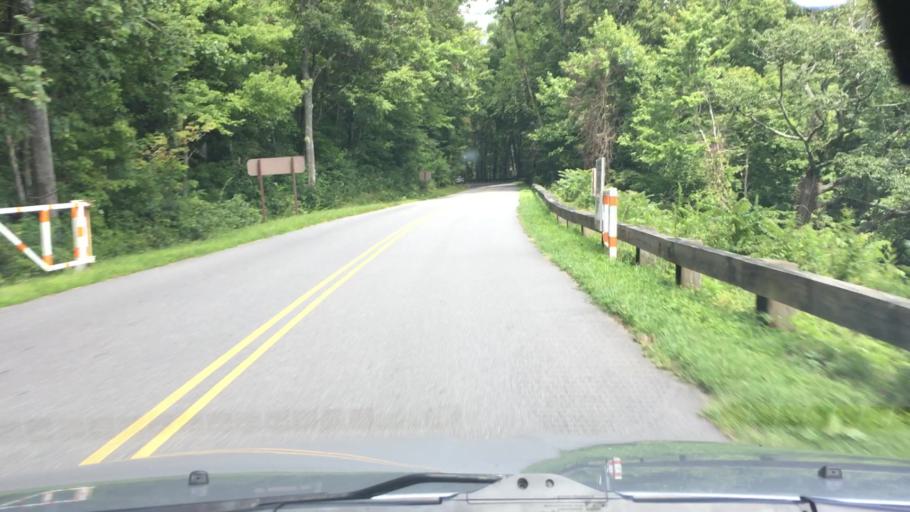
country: US
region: North Carolina
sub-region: Buncombe County
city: Weaverville
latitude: 35.6644
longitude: -82.4780
